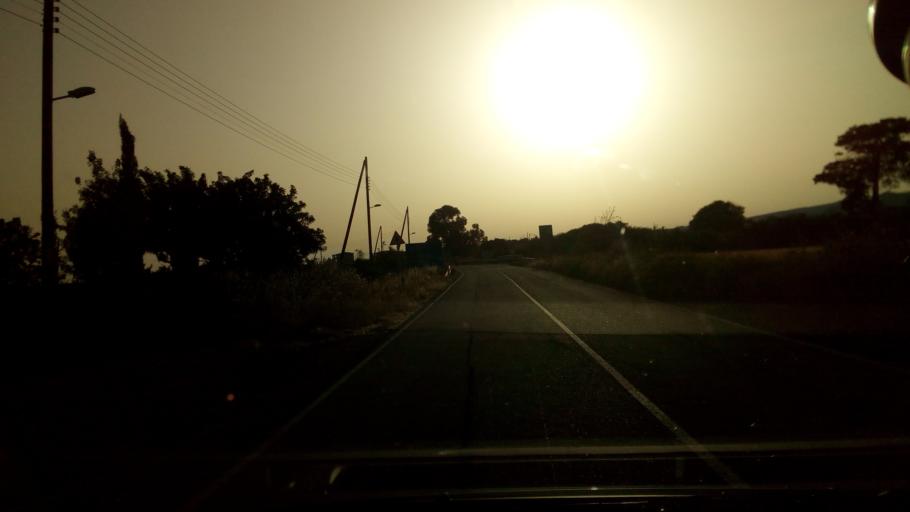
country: CY
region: Larnaka
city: Kofinou
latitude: 34.7517
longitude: 33.4115
